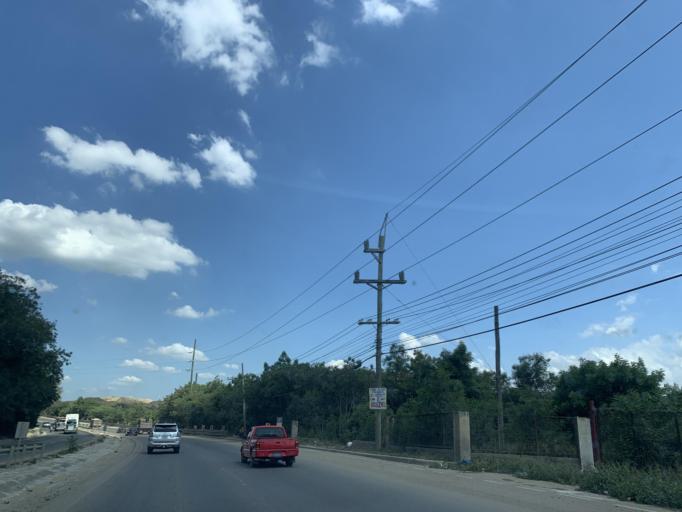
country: DO
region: Santiago
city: Villa Bisono
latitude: 19.5493
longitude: -70.8542
